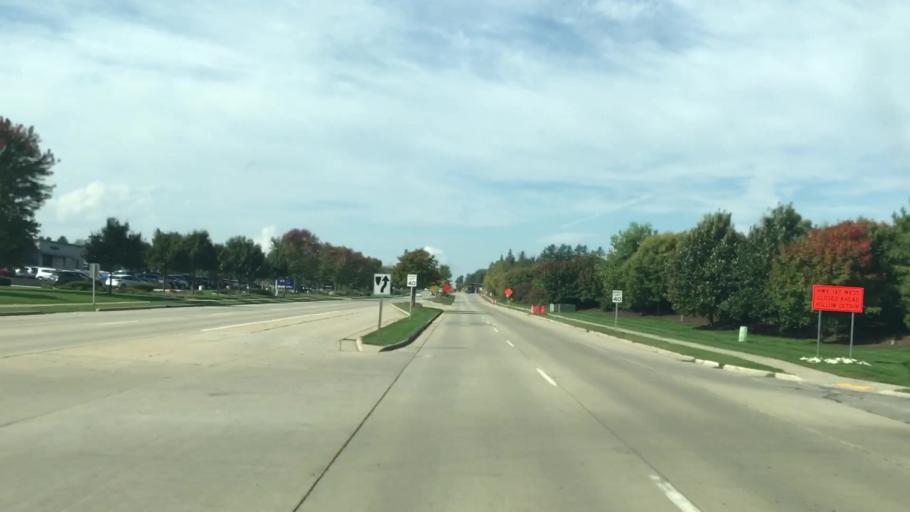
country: US
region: Wisconsin
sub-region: Ozaukee County
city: Mequon
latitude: 43.2217
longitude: -87.9973
